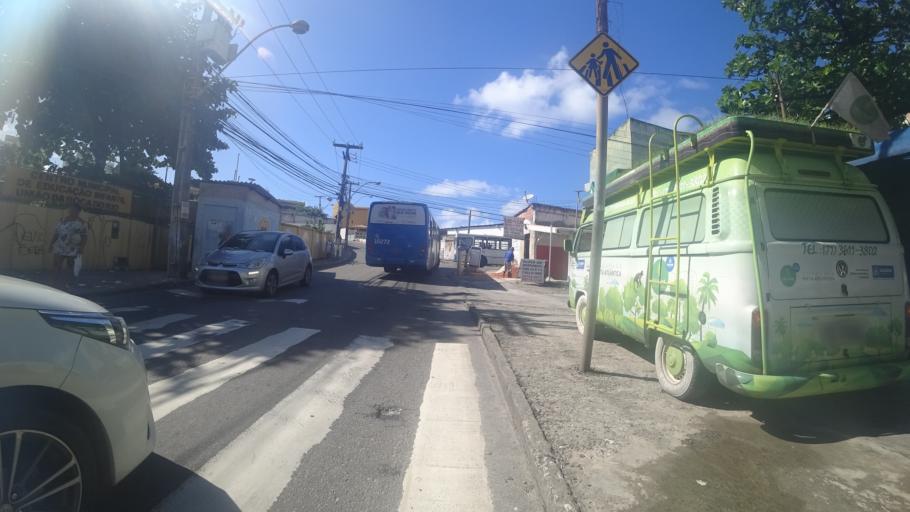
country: BR
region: Bahia
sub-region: Salvador
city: Salvador
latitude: -12.9737
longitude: -38.4337
